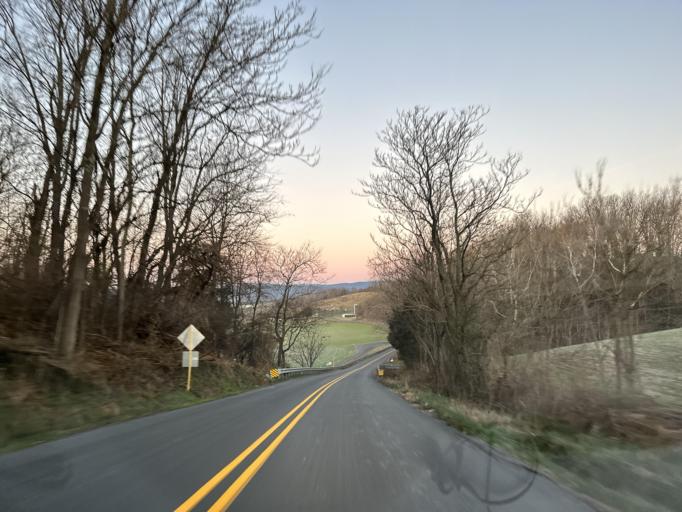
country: US
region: Virginia
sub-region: Rockingham County
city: Bridgewater
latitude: 38.3942
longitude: -79.0411
